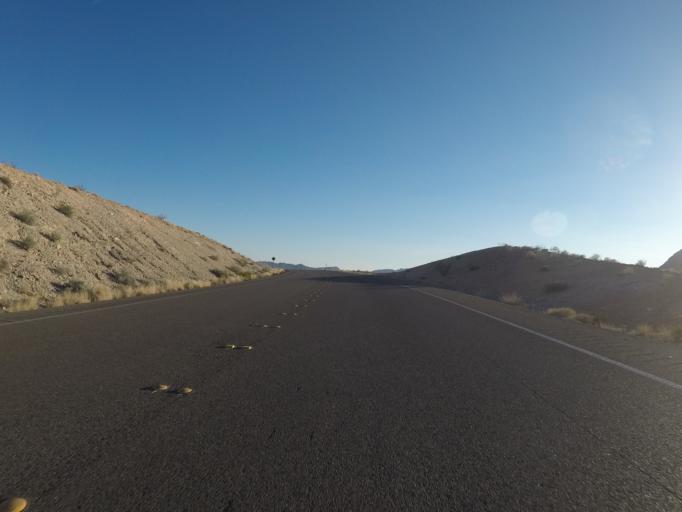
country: US
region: Nevada
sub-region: Clark County
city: Moapa Valley
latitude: 36.3587
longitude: -114.4838
